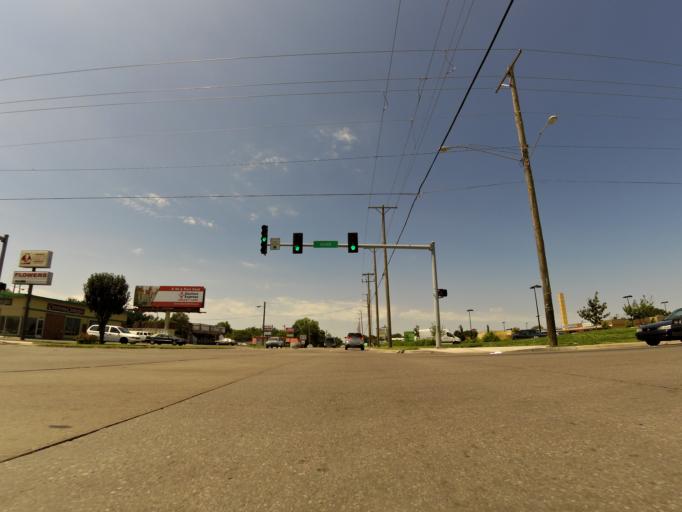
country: US
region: Kansas
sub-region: Sedgwick County
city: Bellaire
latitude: 37.7084
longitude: -97.2805
